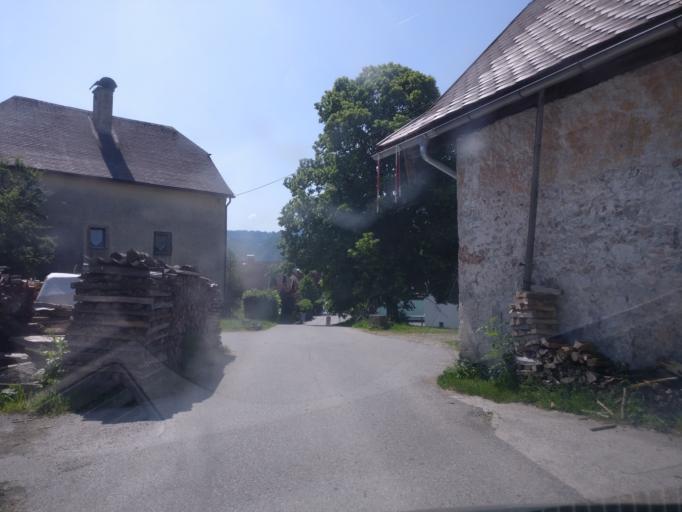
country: AT
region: Salzburg
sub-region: Politischer Bezirk Hallein
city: Oberalm
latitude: 47.6959
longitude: 13.0875
